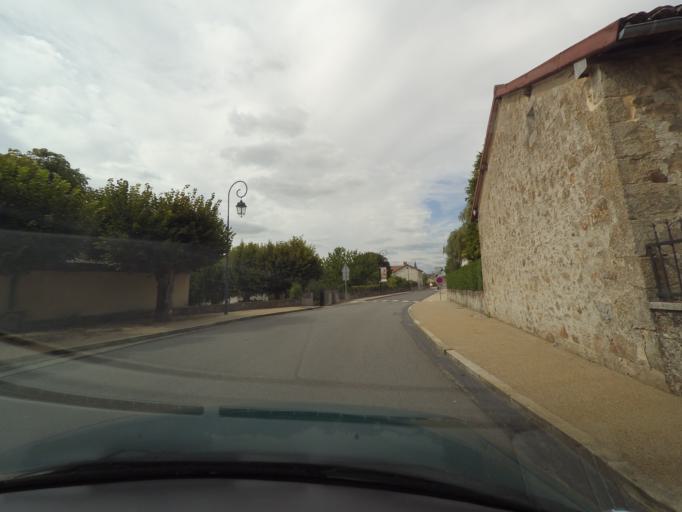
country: FR
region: Limousin
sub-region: Departement de la Haute-Vienne
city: Bussiere-Galant
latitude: 45.6783
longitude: 1.0735
